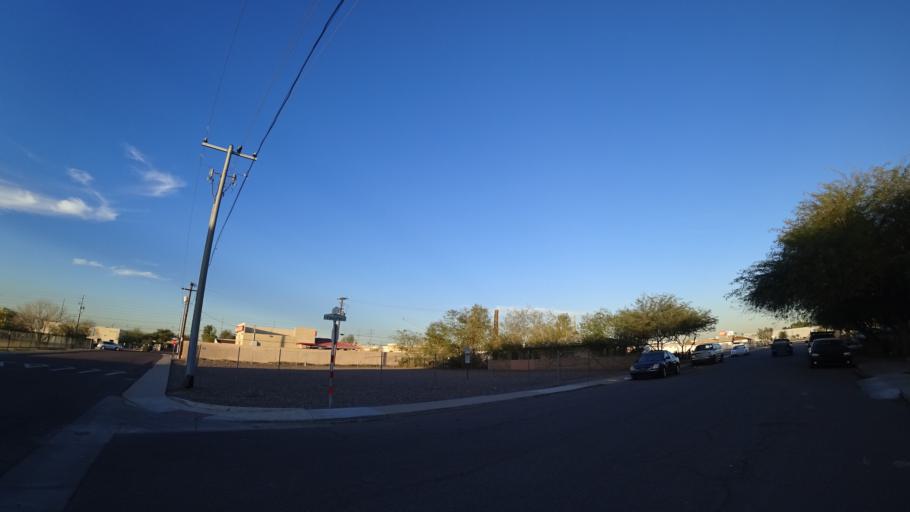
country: US
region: Arizona
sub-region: Maricopa County
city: Phoenix
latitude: 33.4358
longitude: -112.0587
